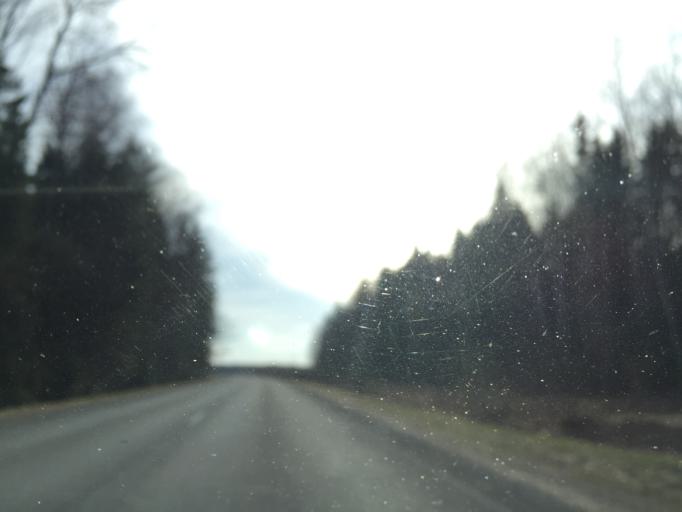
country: LV
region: Lielvarde
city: Lielvarde
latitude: 56.7937
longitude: 24.8146
